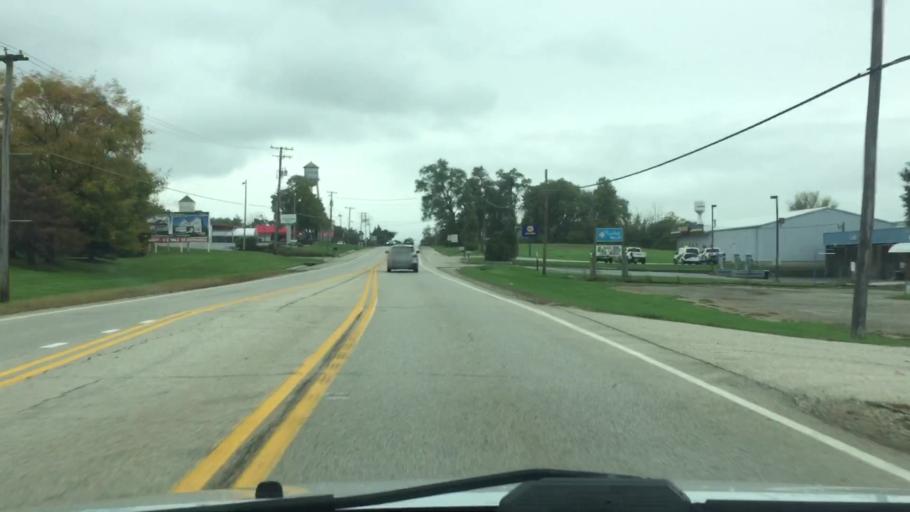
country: US
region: Illinois
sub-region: McHenry County
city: Richmond
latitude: 42.4861
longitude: -88.3062
